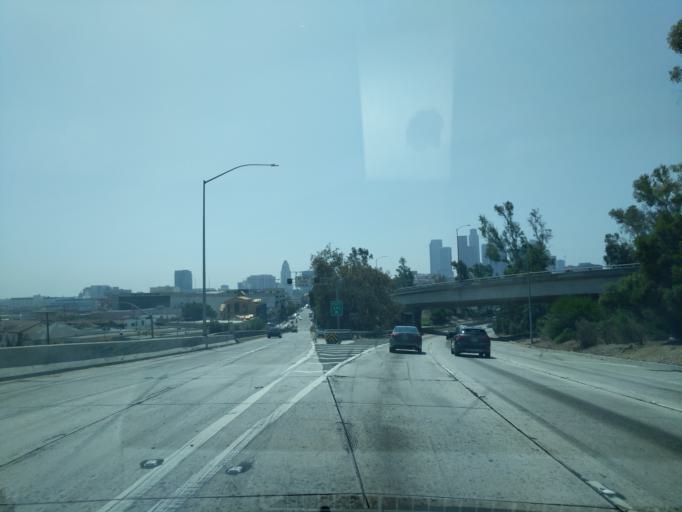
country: US
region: California
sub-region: Los Angeles County
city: Los Angeles
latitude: 34.0695
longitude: -118.2363
